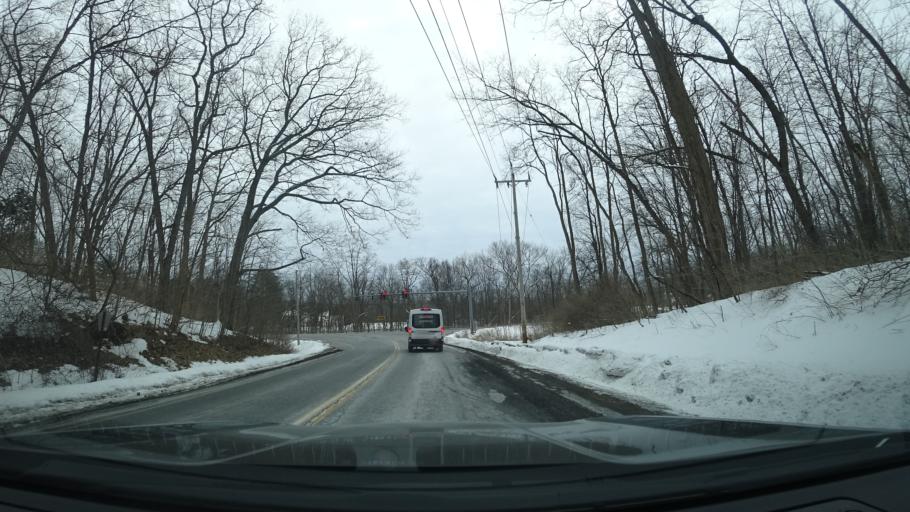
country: US
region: New York
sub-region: Washington County
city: Fort Edward
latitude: 43.2604
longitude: -73.5955
